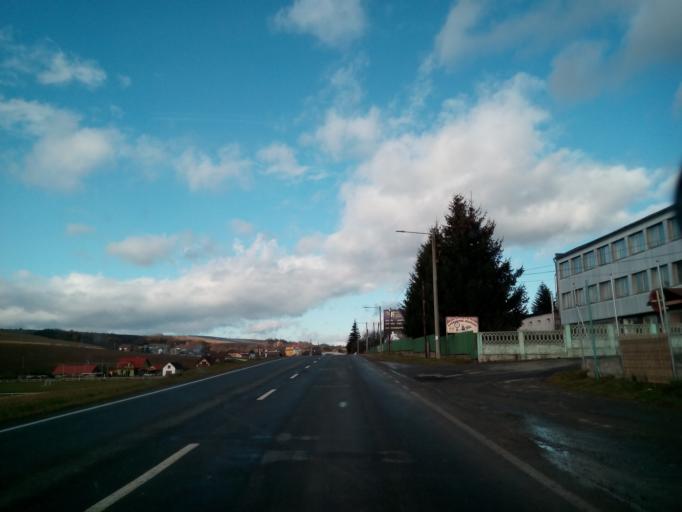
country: SK
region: Presovsky
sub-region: Okres Bardejov
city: Bardejov
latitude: 49.2093
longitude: 21.3027
